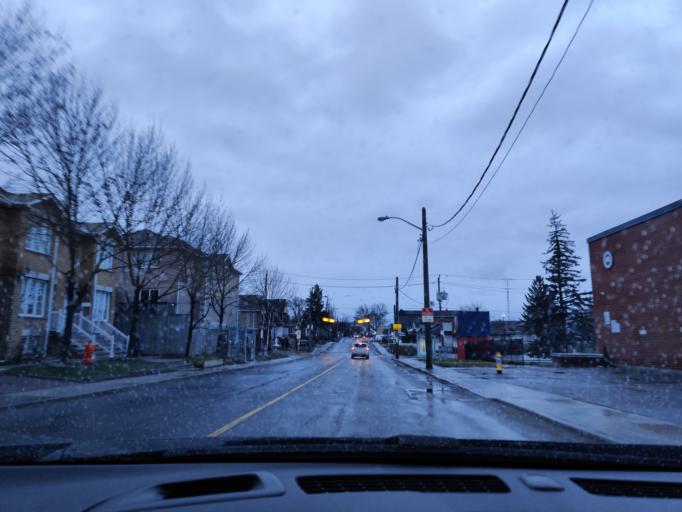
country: CA
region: Ontario
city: Toronto
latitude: 43.6956
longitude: -79.4631
